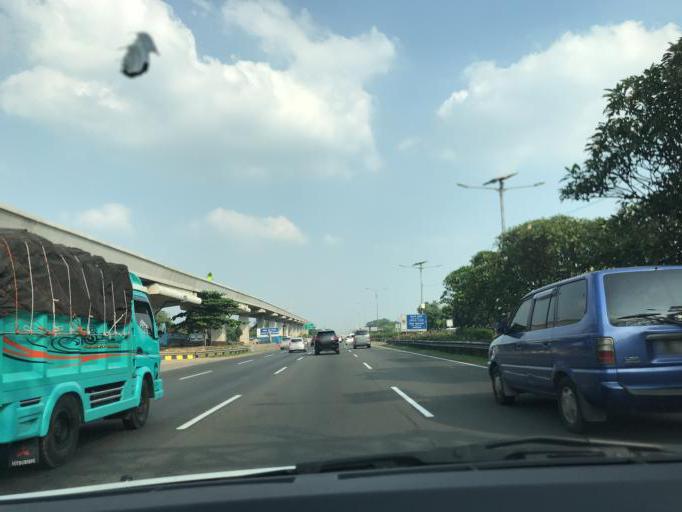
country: ID
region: Jakarta Raya
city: Jakarta
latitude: -6.2790
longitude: 106.8746
